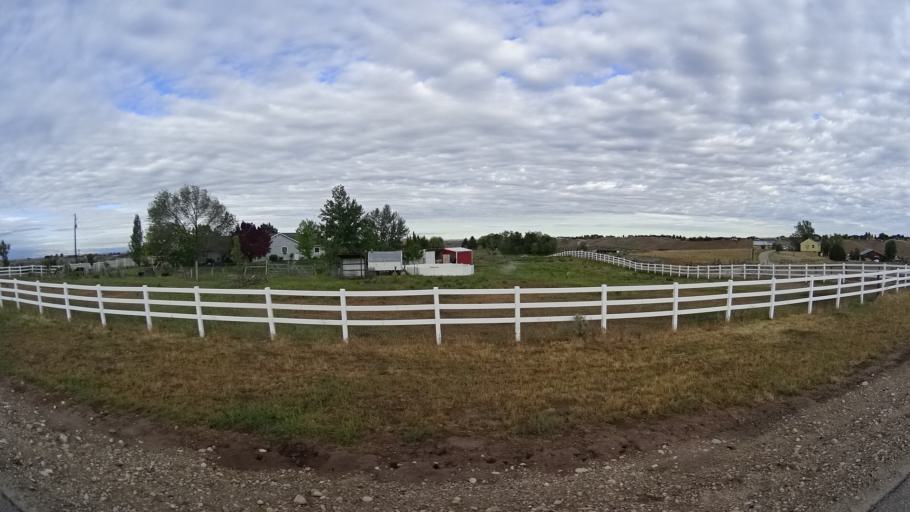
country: US
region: Idaho
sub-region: Ada County
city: Star
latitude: 43.7329
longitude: -116.5128
